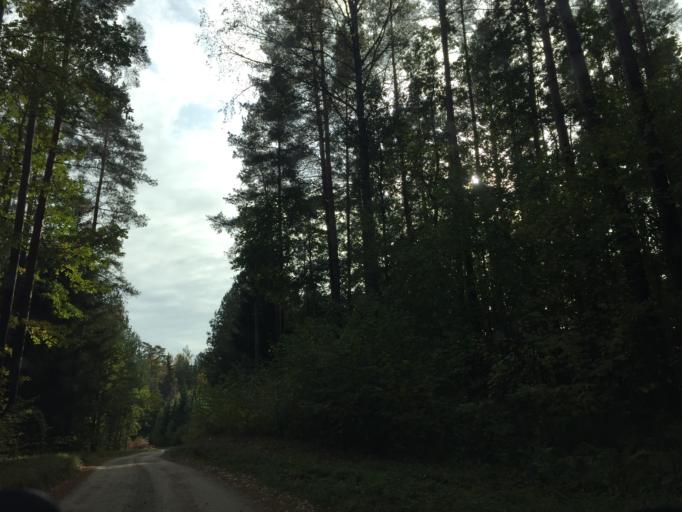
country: LV
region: Jaunpils
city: Jaunpils
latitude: 56.5798
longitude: 23.0245
